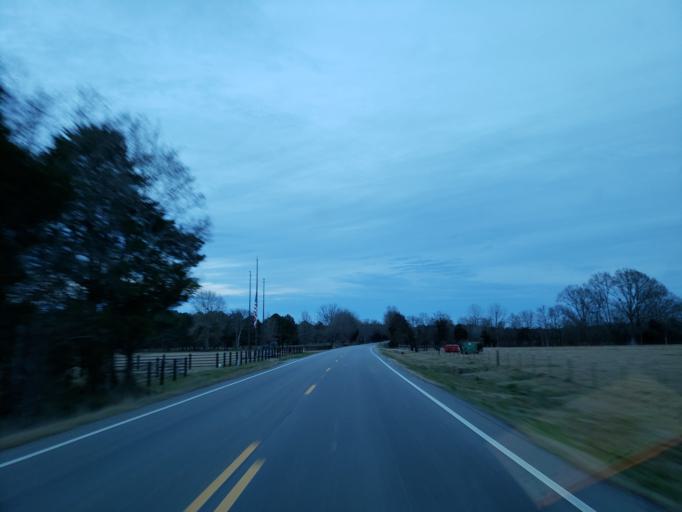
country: US
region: Alabama
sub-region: Sumter County
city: Livingston
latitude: 32.8113
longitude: -88.2547
